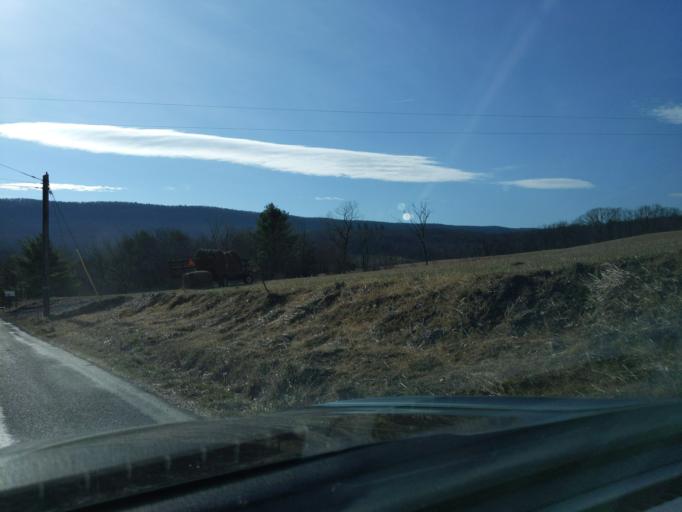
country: US
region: Pennsylvania
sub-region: Blair County
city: Hollidaysburg
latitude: 40.4101
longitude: -78.3266
